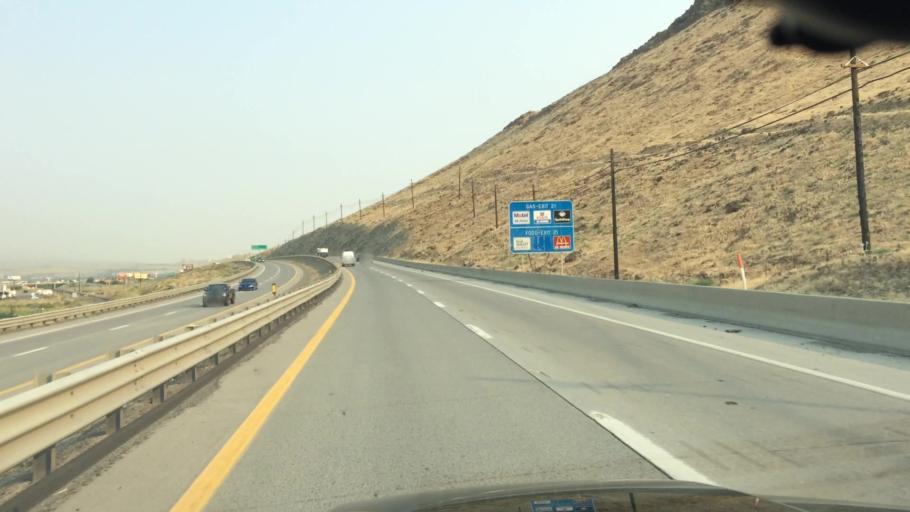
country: US
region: Nevada
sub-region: Washoe County
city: Sparks
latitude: 39.5206
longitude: -119.6865
